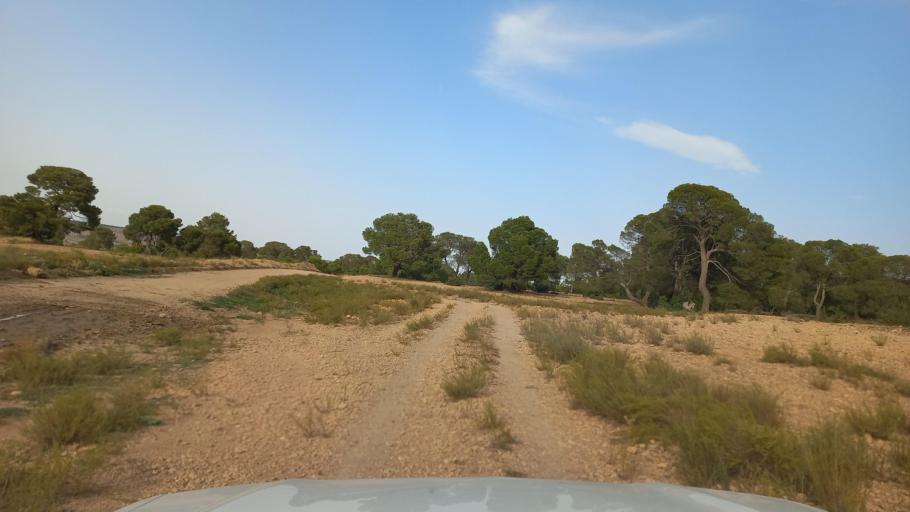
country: TN
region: Al Qasrayn
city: Kasserine
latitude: 35.3353
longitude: 8.8530
